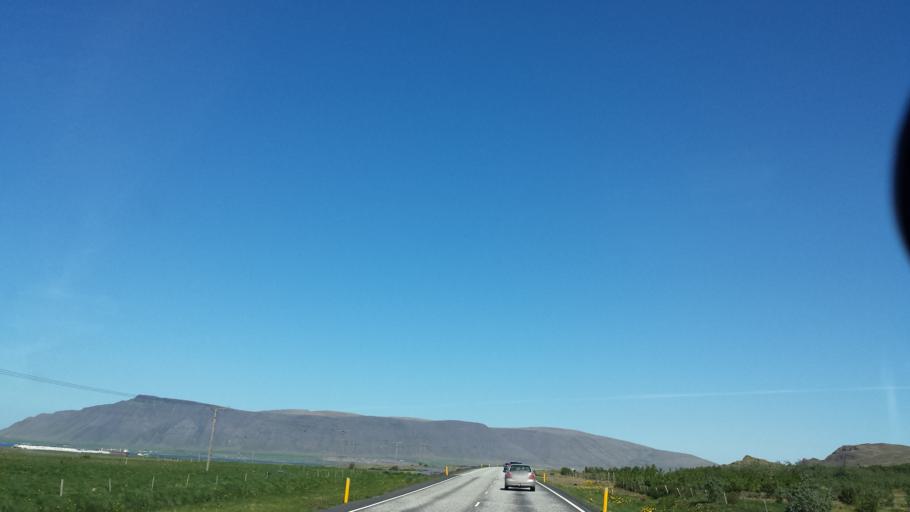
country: IS
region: Capital Region
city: Reykjavik
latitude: 64.2547
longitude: -21.8305
